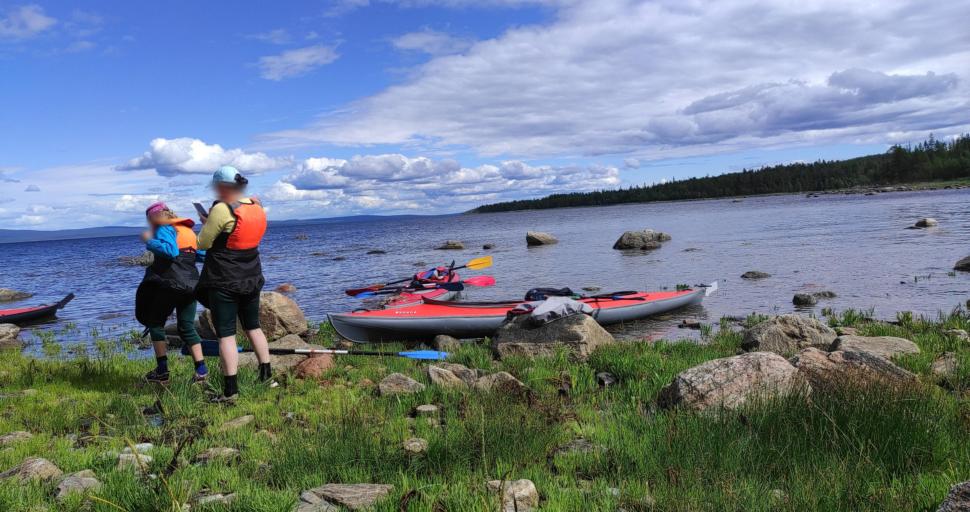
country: RU
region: Murmansk
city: Poyakonda
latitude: 66.7720
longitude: 32.8066
